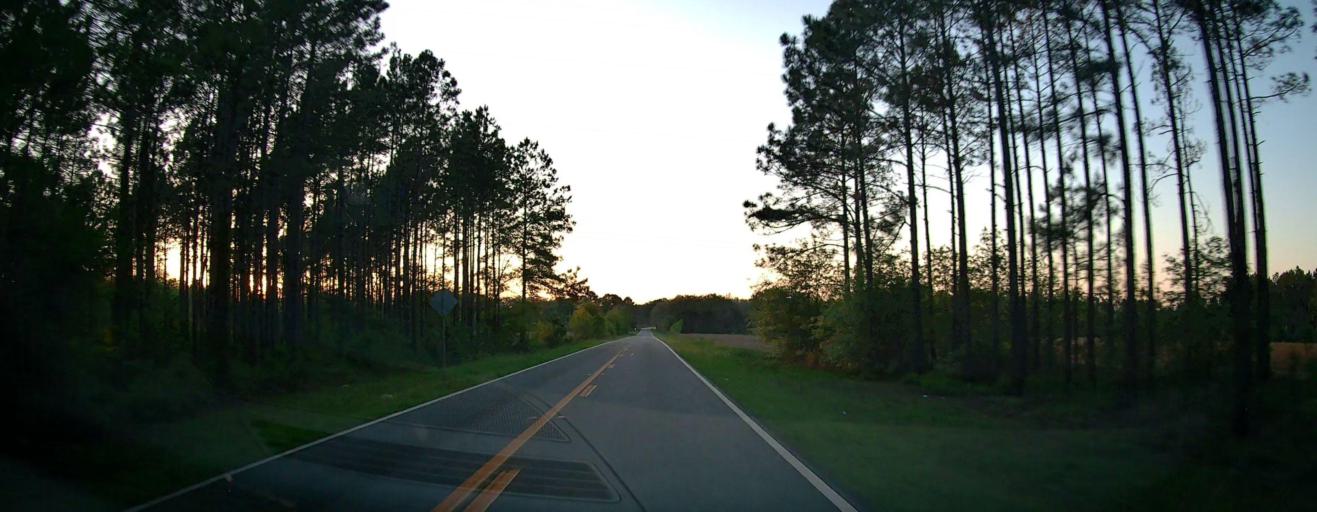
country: US
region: Georgia
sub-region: Wilcox County
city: Rochelle
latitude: 31.7962
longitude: -83.4459
